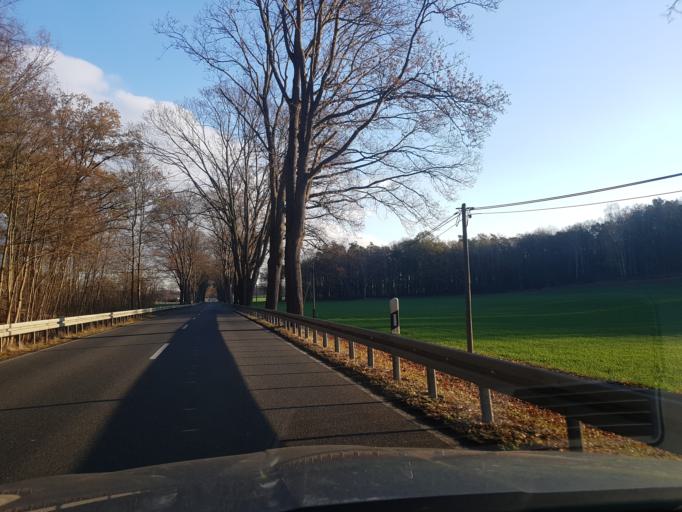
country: DE
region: Brandenburg
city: Luckau
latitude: 51.8246
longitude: 13.6152
